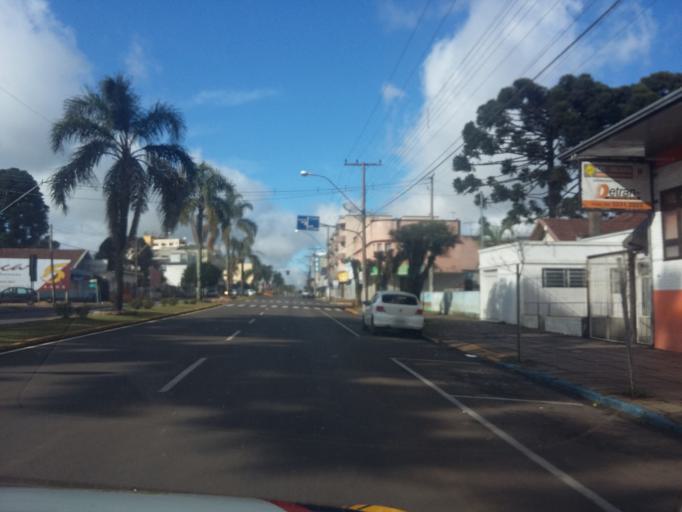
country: BR
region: Rio Grande do Sul
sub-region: Vacaria
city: Vacaria
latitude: -28.5088
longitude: -50.9363
